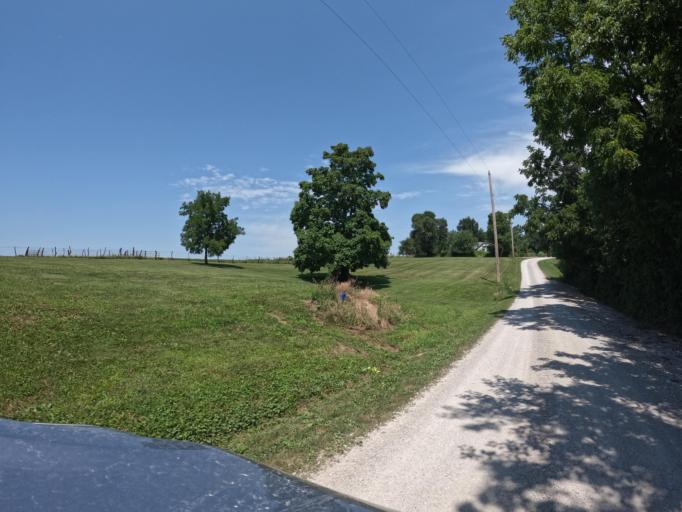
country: US
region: Iowa
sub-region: Appanoose County
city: Centerville
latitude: 40.7817
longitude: -92.9495
